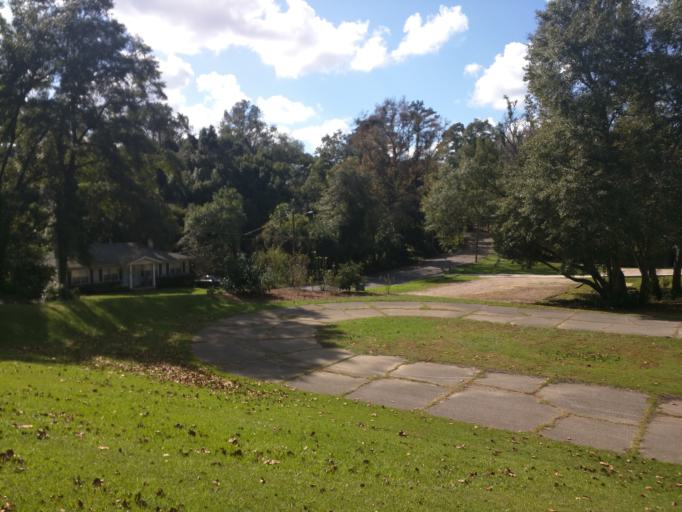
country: US
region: Florida
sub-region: Leon County
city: Tallahassee
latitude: 30.4521
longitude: -84.2731
